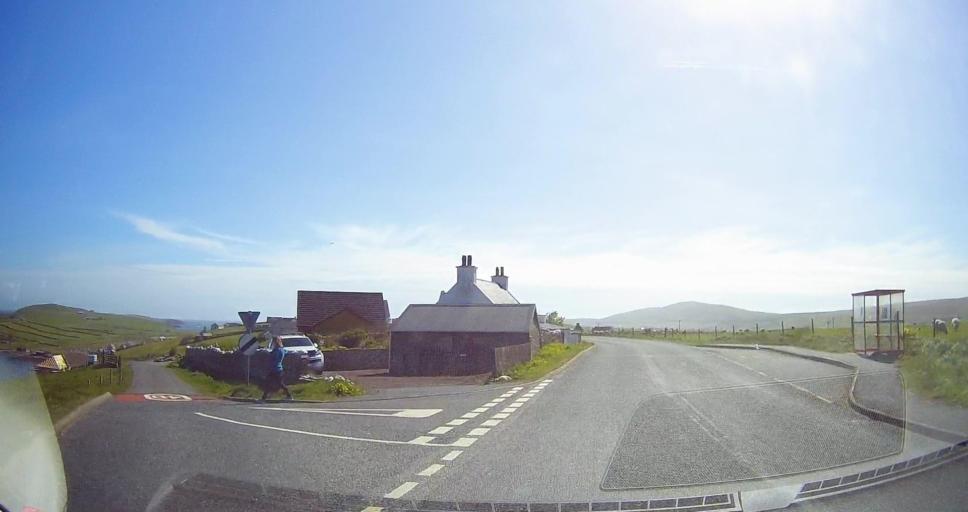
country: GB
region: Scotland
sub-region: Shetland Islands
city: Sandwick
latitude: 60.0121
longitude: -1.2267
